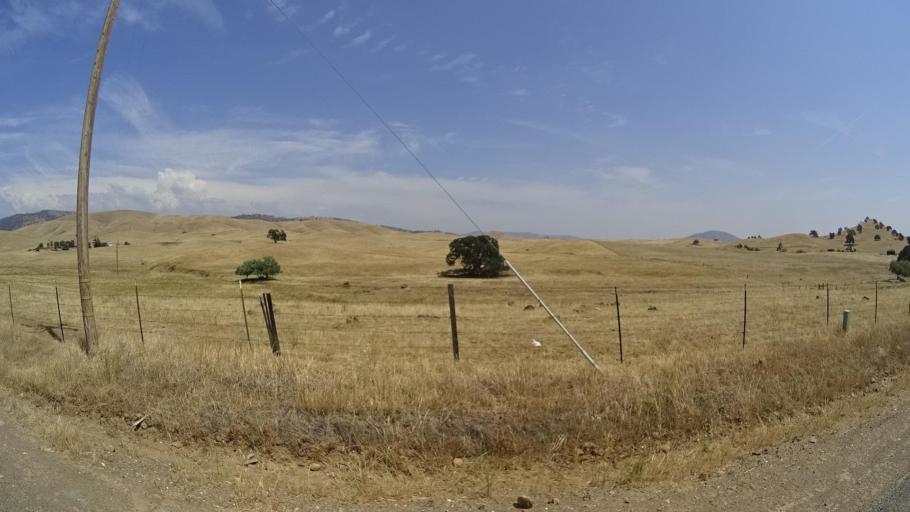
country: US
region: California
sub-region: Mariposa County
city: Mariposa
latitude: 37.5308
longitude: -120.2087
